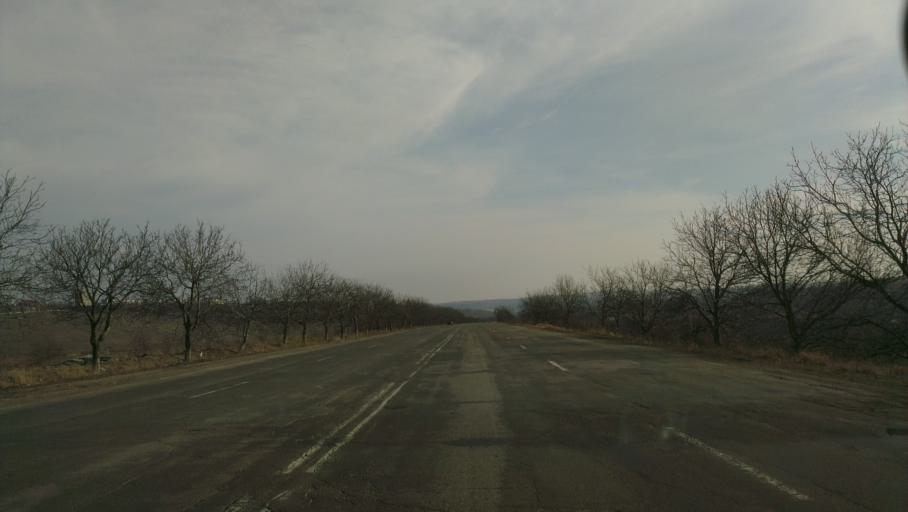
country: MD
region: Laloveni
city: Ialoveni
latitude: 46.9784
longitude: 28.7479
